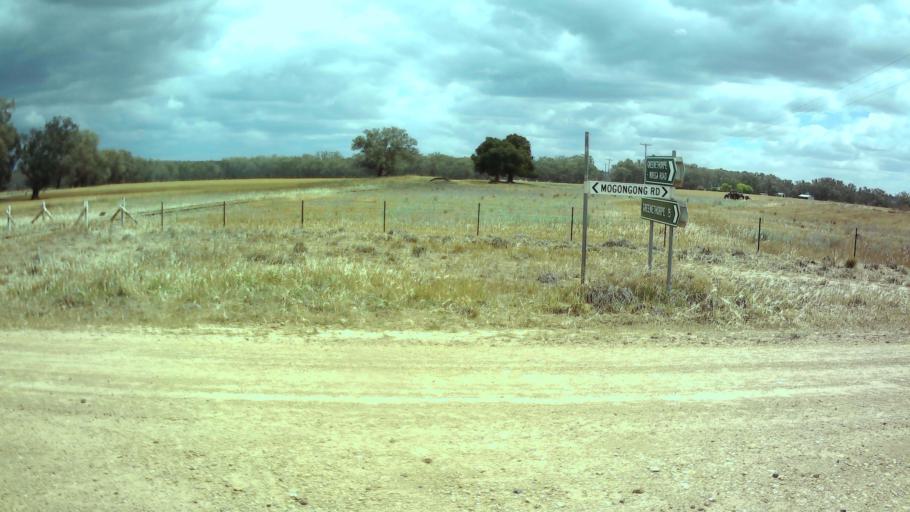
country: AU
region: New South Wales
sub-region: Weddin
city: Grenfell
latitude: -33.9330
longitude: 148.2790
